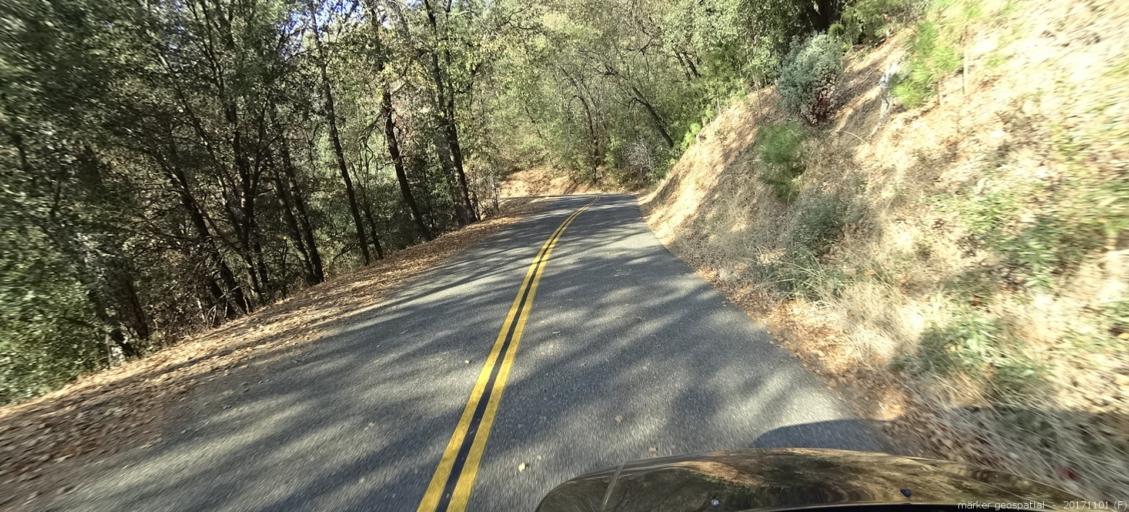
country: US
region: California
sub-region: Shasta County
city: Shasta Lake
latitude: 40.8053
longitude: -122.3070
